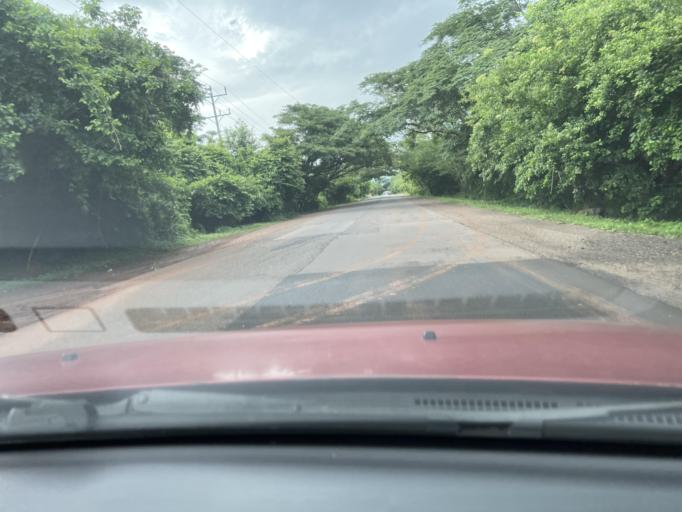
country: SV
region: La Union
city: San Alejo
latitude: 13.4073
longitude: -87.8922
